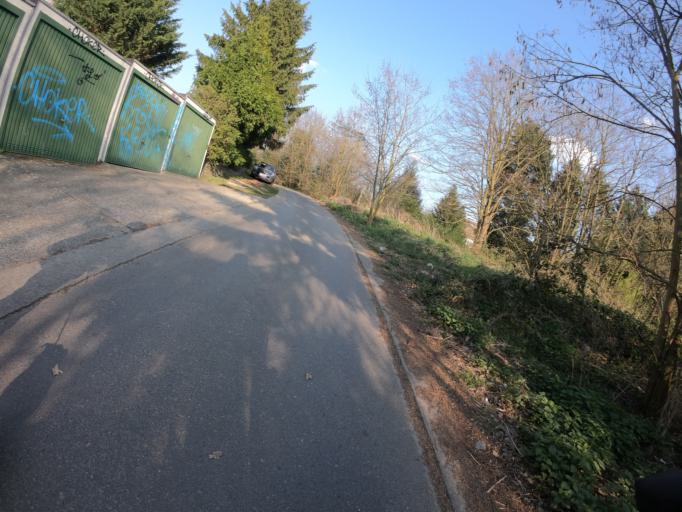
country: BE
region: Flanders
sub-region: Provincie Vlaams-Brabant
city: Kraainem
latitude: 50.8448
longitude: 4.4548
